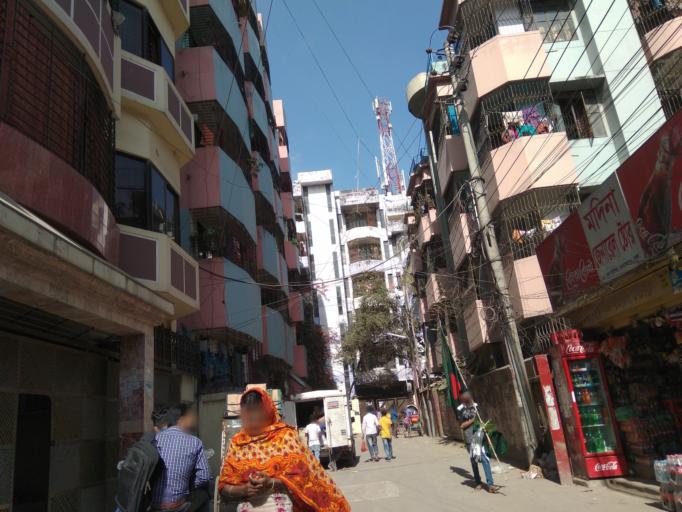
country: BD
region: Dhaka
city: Azimpur
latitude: 23.7751
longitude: 90.3594
